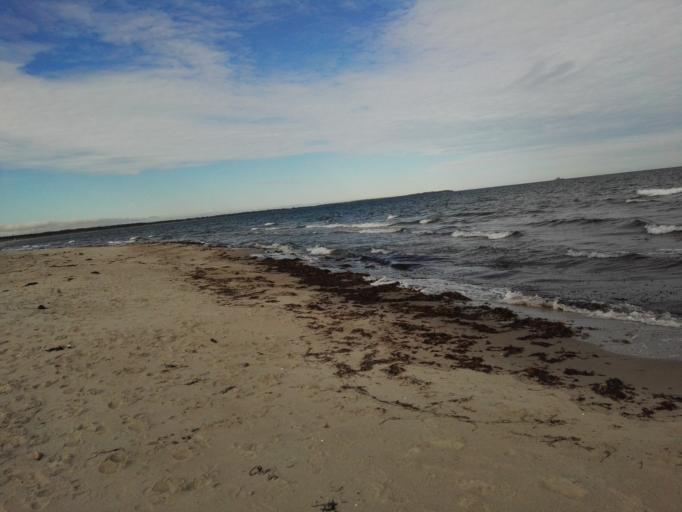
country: DK
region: Zealand
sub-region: Odsherred Kommune
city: Nykobing Sjaelland
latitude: 55.9638
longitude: 11.7374
